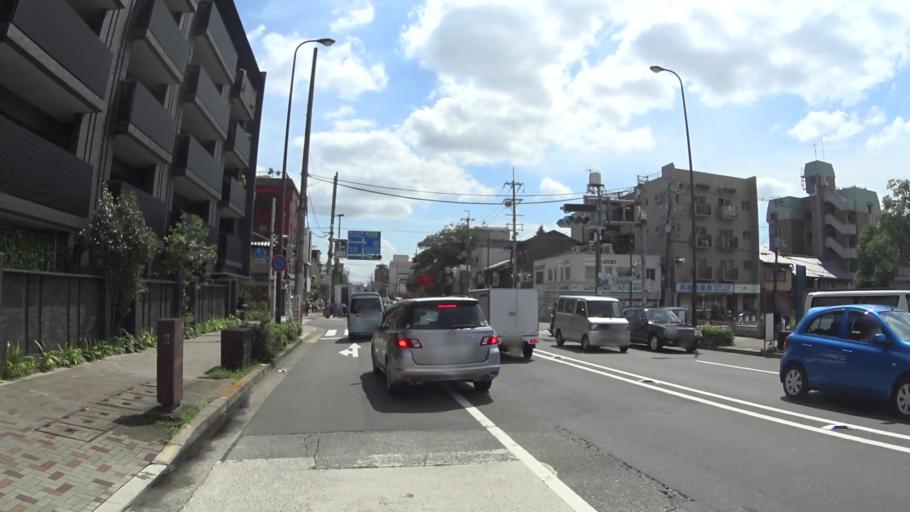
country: JP
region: Kyoto
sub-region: Kyoto-shi
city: Kamigyo-ku
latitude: 35.0189
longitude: 135.7786
